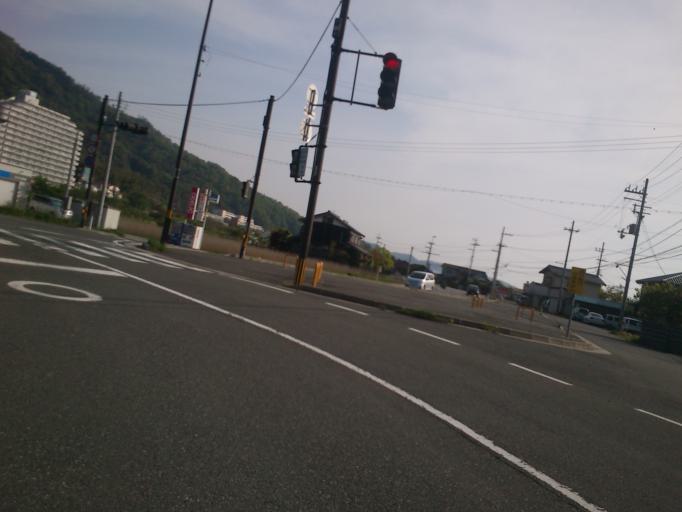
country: JP
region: Kyoto
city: Miyazu
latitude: 35.5836
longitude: 135.2043
